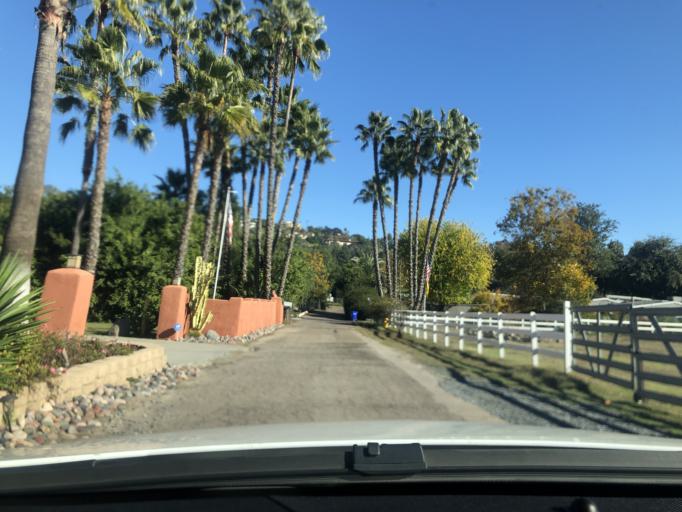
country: US
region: California
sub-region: San Diego County
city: El Cajon
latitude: 32.7769
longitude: -116.9428
